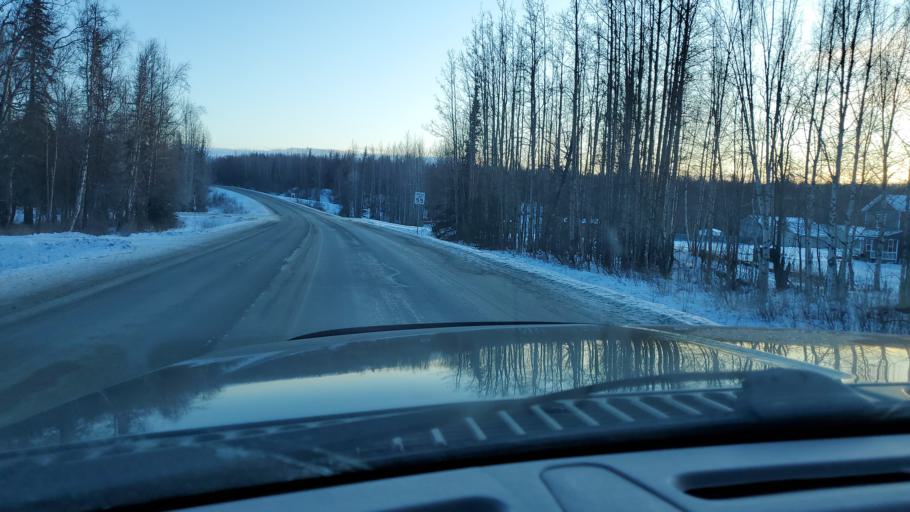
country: US
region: Alaska
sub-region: Matanuska-Susitna Borough
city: Fishhook
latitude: 61.6841
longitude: -149.2395
